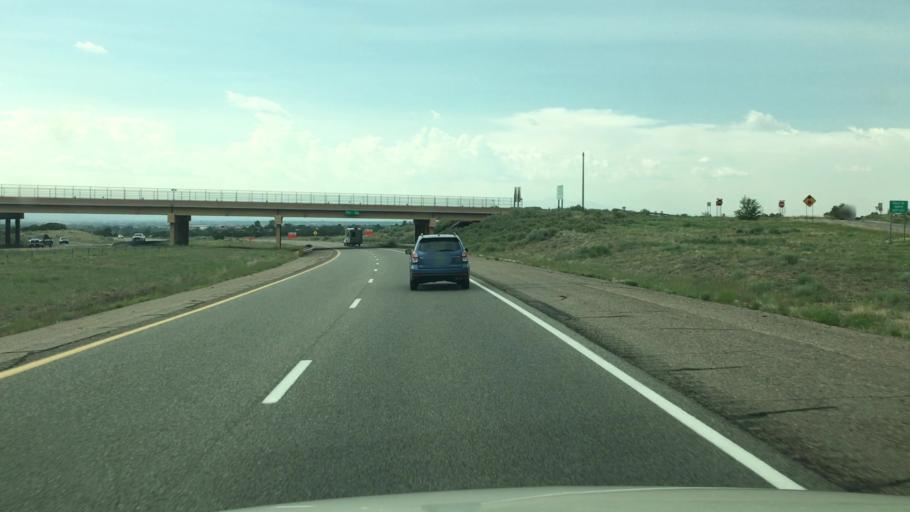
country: US
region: New Mexico
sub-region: Santa Fe County
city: Santa Fe
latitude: 35.6359
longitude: -105.9289
